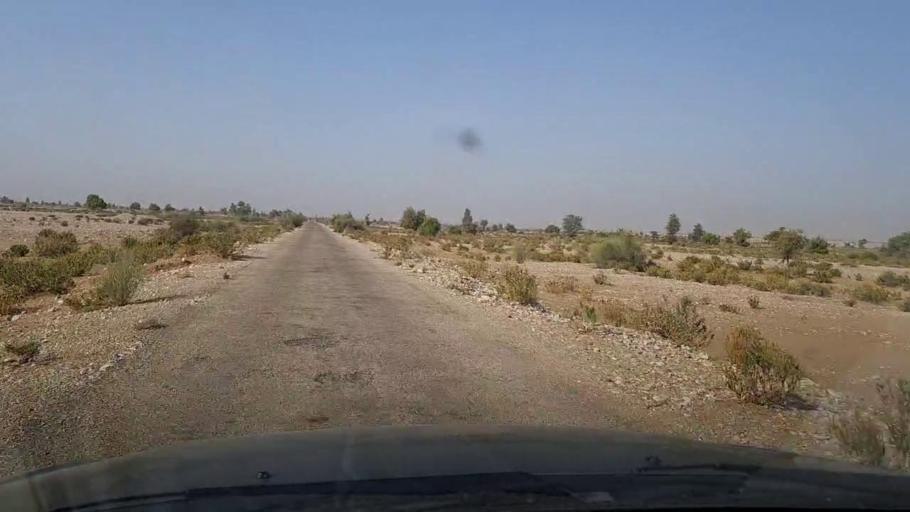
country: PK
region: Sindh
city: Sann
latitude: 25.9576
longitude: 68.0429
